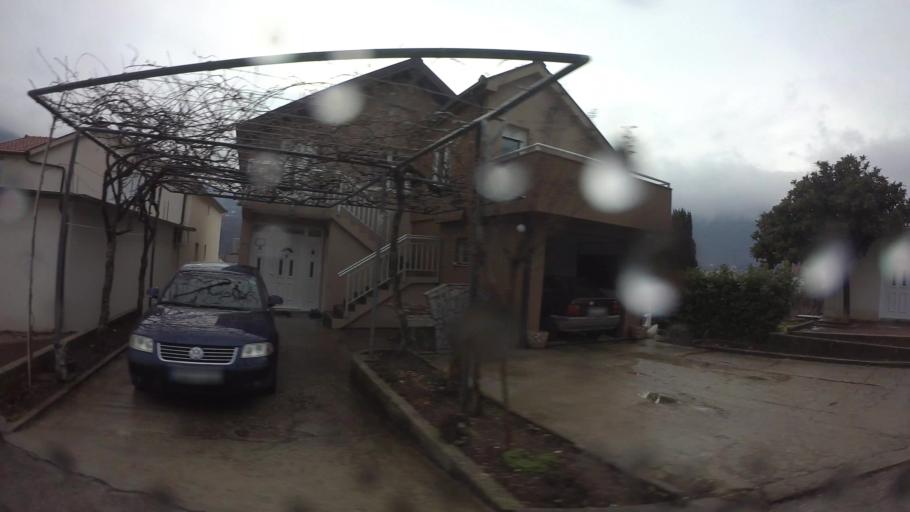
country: BA
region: Federation of Bosnia and Herzegovina
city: Cim
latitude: 43.3491
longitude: 17.7767
